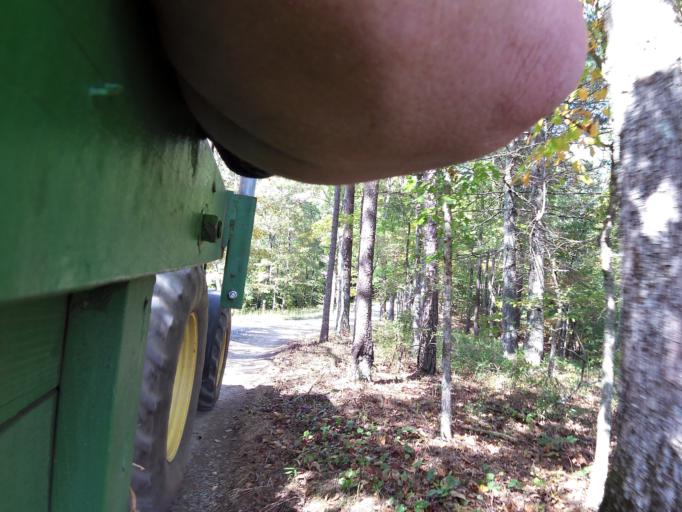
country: US
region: Georgia
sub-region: Dawson County
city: Dawsonville
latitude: 34.5479
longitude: -84.2544
